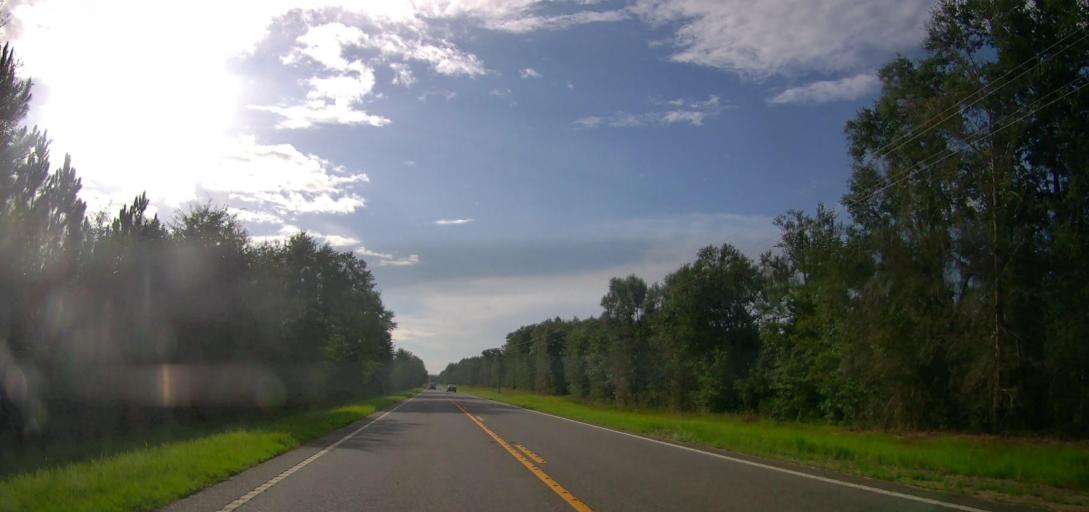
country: US
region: Georgia
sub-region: Coffee County
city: Nicholls
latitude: 31.3343
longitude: -82.5925
